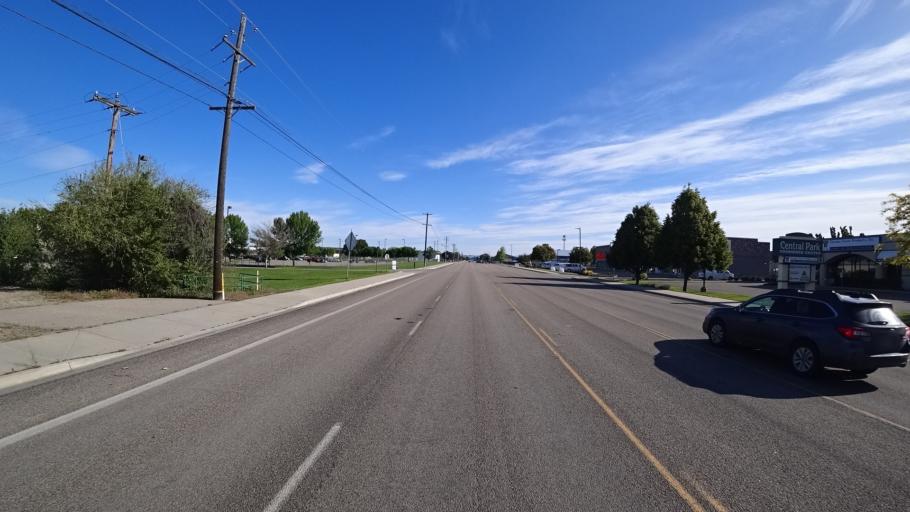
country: US
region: Idaho
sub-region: Ada County
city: Garden City
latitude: 43.5806
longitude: -116.2742
